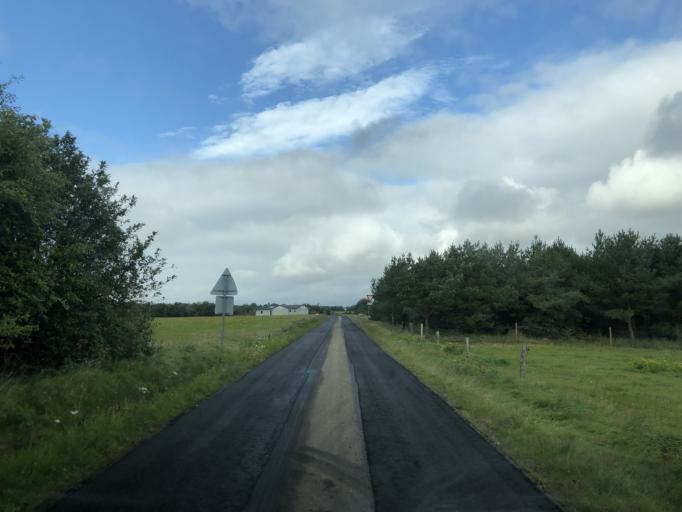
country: DK
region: Central Jutland
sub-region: Holstebro Kommune
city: Ulfborg
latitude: 56.3118
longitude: 8.4263
